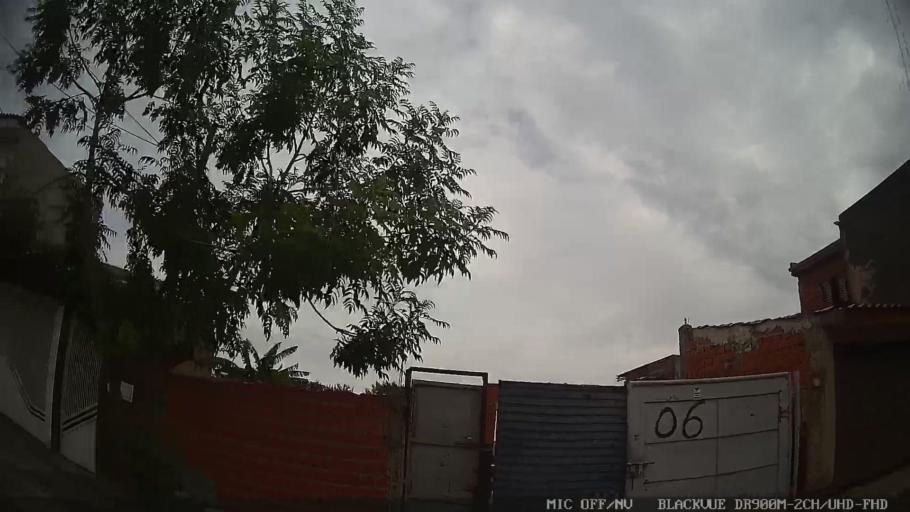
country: BR
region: Sao Paulo
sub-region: Salto
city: Salto
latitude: -23.2181
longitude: -47.2764
